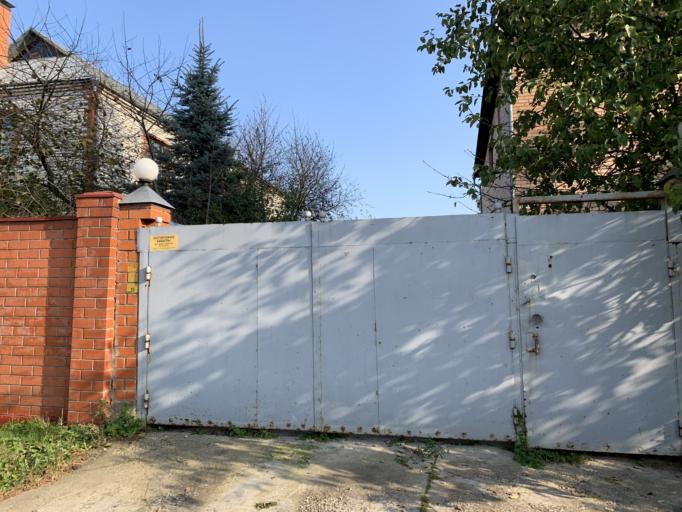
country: RU
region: Moskovskaya
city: Lesnyye Polyany
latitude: 55.9666
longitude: 37.8457
